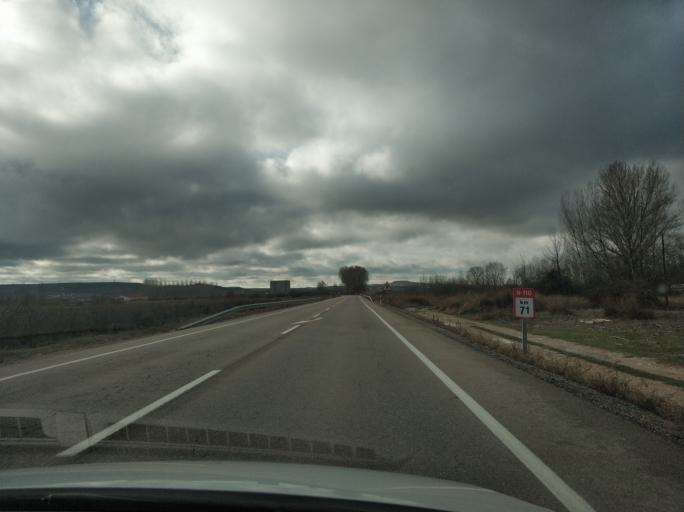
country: ES
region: Castille and Leon
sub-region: Provincia de Soria
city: San Esteban de Gormaz
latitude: 41.5706
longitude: -3.2148
